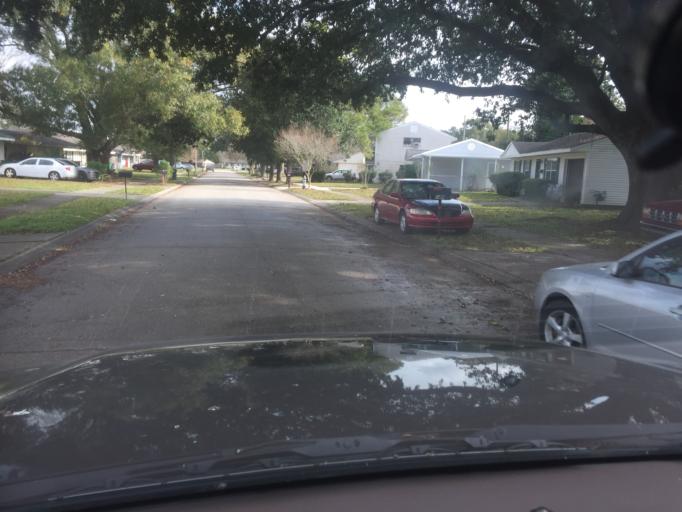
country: US
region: Louisiana
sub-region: Jefferson Parish
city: Avondale
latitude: 29.9133
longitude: -90.2041
